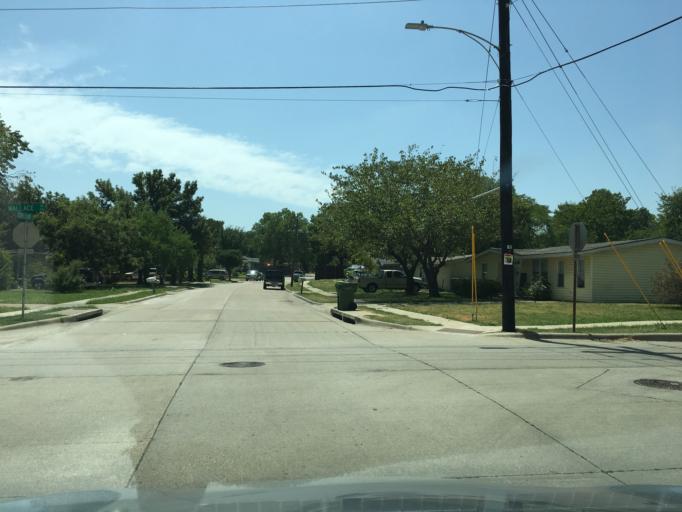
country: US
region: Texas
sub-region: Dallas County
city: Garland
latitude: 32.8925
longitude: -96.6259
